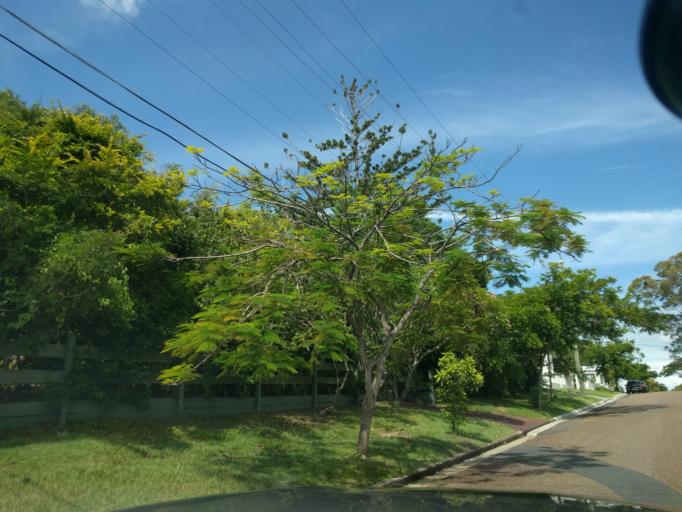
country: AU
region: Queensland
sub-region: Brisbane
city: Wilston
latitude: -27.4379
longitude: 153.0177
